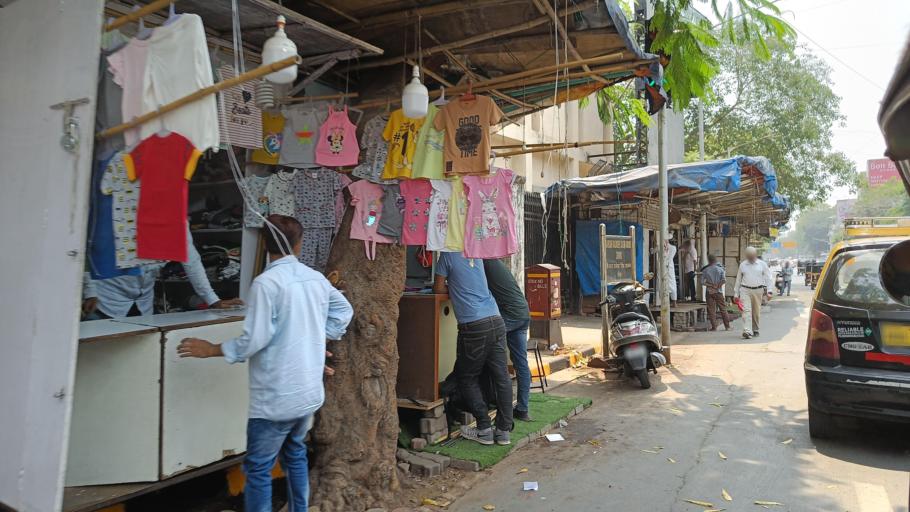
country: IN
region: Maharashtra
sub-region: Mumbai Suburban
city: Mumbai
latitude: 19.0675
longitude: 72.8336
